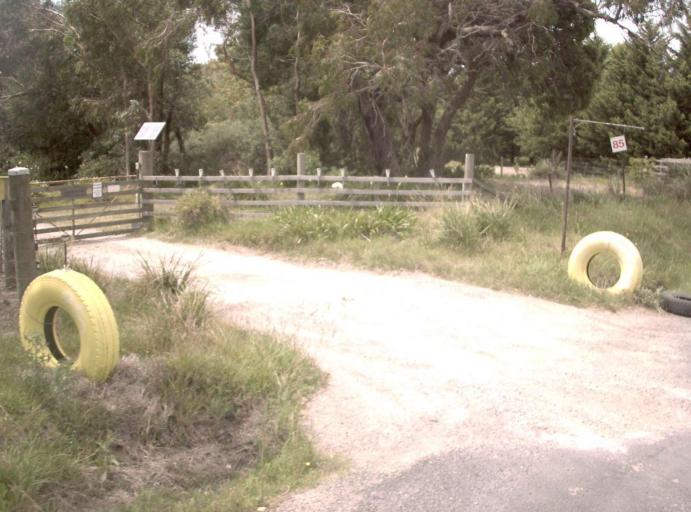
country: AU
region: Victoria
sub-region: Mornington Peninsula
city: Tyabb
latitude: -38.2287
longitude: 145.2168
